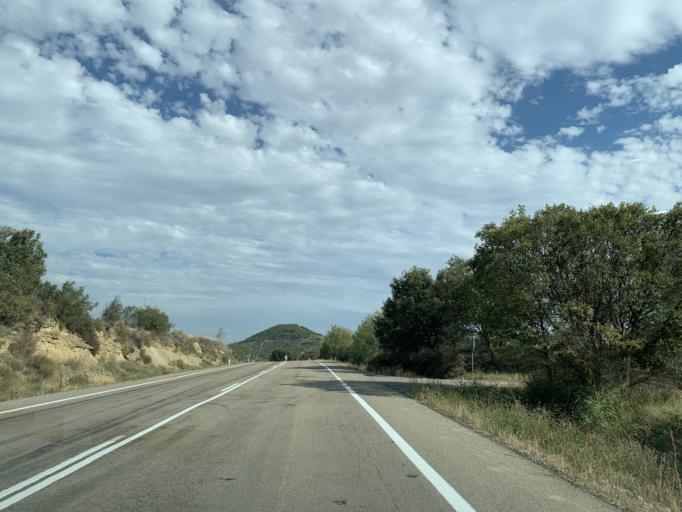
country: ES
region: Aragon
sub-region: Provincia de Huesca
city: Ayerbe
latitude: 42.2874
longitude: -0.7125
